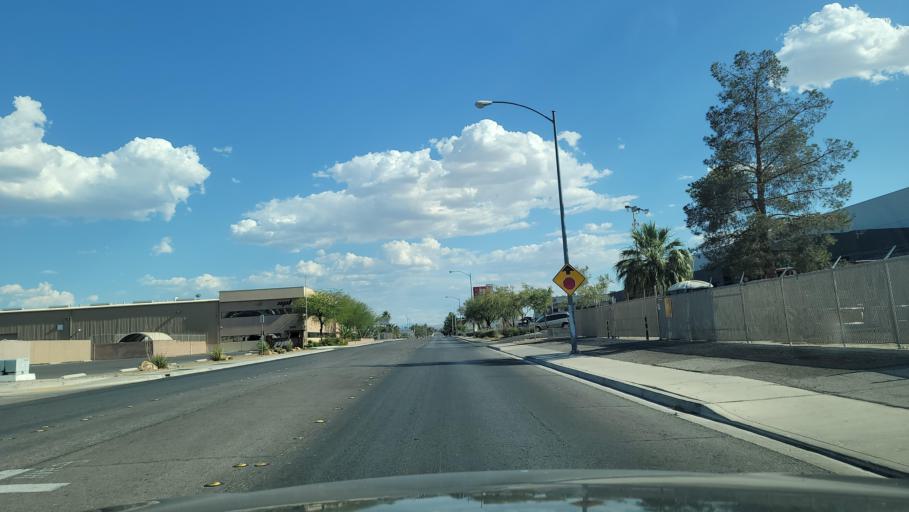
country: US
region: Nevada
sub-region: Clark County
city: Spring Valley
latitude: 36.0987
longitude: -115.2040
